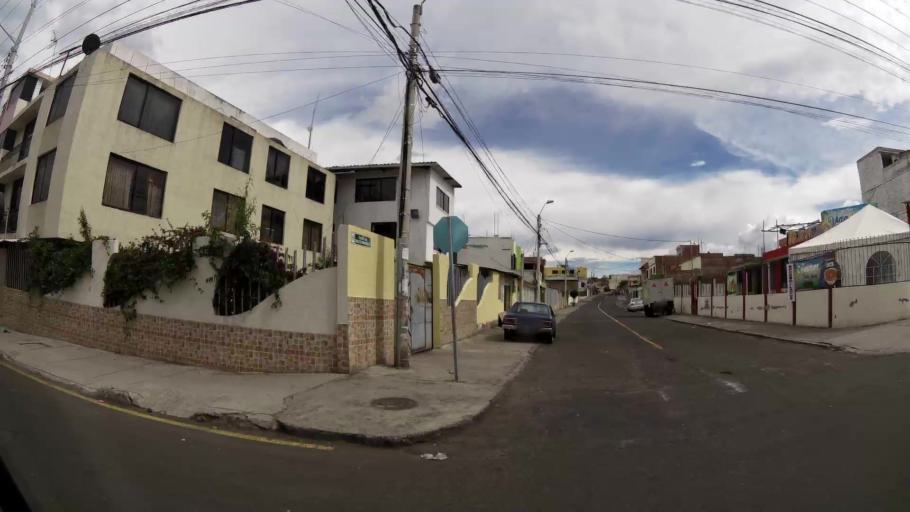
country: EC
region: Tungurahua
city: Ambato
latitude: -1.2695
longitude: -78.6360
